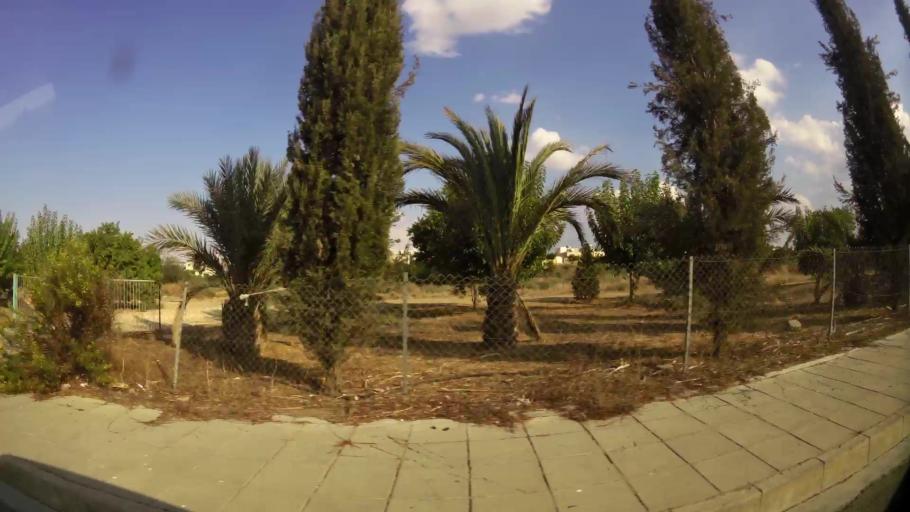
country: CY
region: Lefkosia
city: Kato Deftera
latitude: 35.1083
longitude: 33.2948
